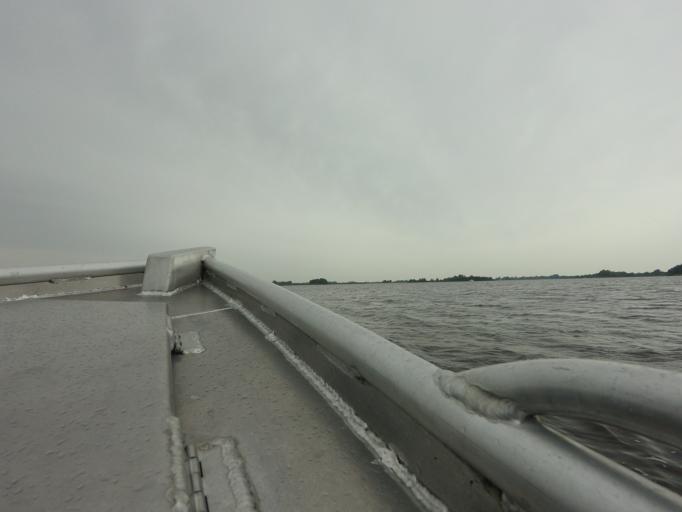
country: NL
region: Overijssel
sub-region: Gemeente Steenwijkerland
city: Blokzijl
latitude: 52.7315
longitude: 6.0077
